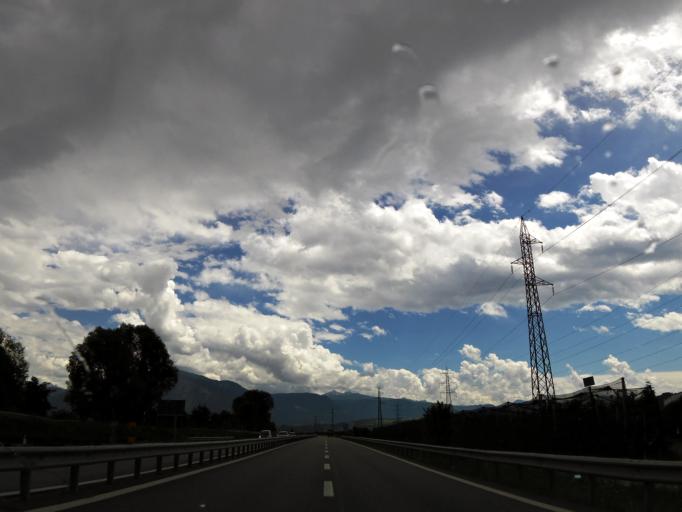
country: IT
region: Trentino-Alto Adige
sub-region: Bolzano
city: Terlano
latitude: 46.5168
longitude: 11.2497
